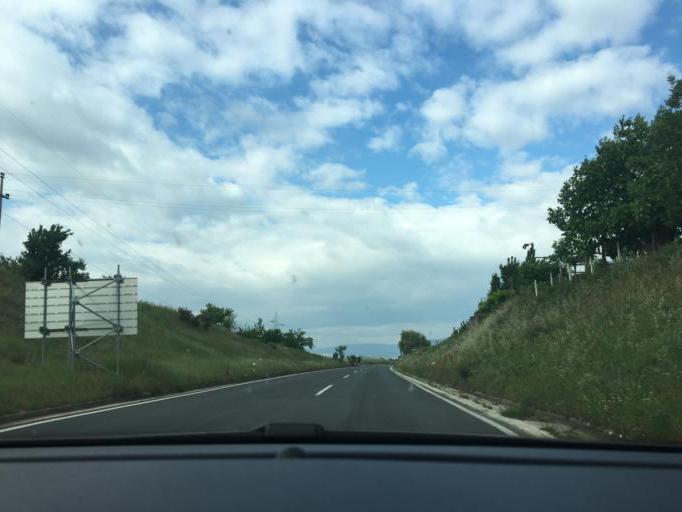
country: MK
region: Prilep
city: Prilep
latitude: 41.3335
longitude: 21.5652
